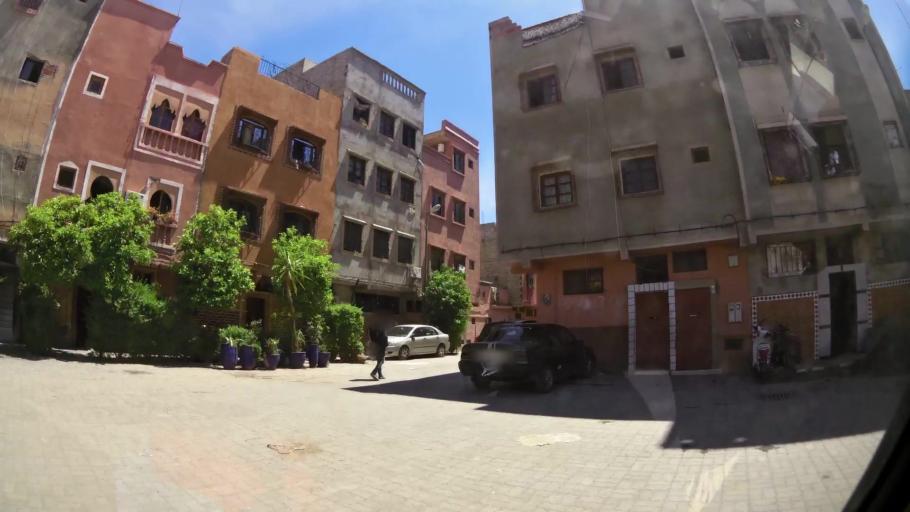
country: MA
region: Marrakech-Tensift-Al Haouz
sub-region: Marrakech
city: Marrakesh
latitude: 31.6551
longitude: -7.9932
